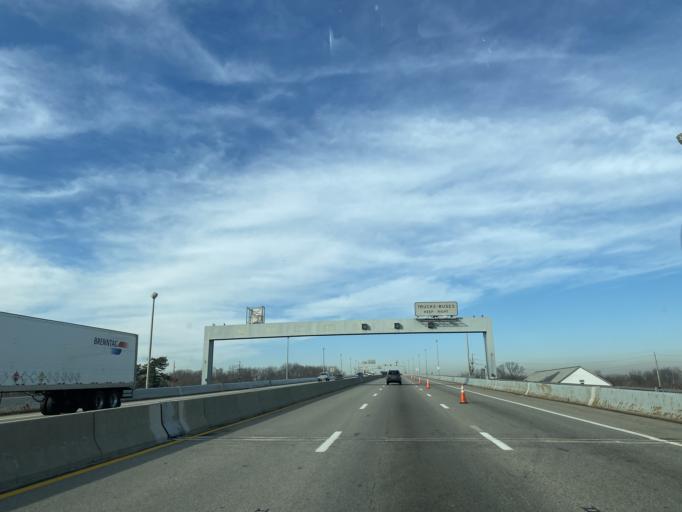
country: US
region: New Jersey
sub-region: Camden County
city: Pennsauken
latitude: 39.9788
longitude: -75.0524
